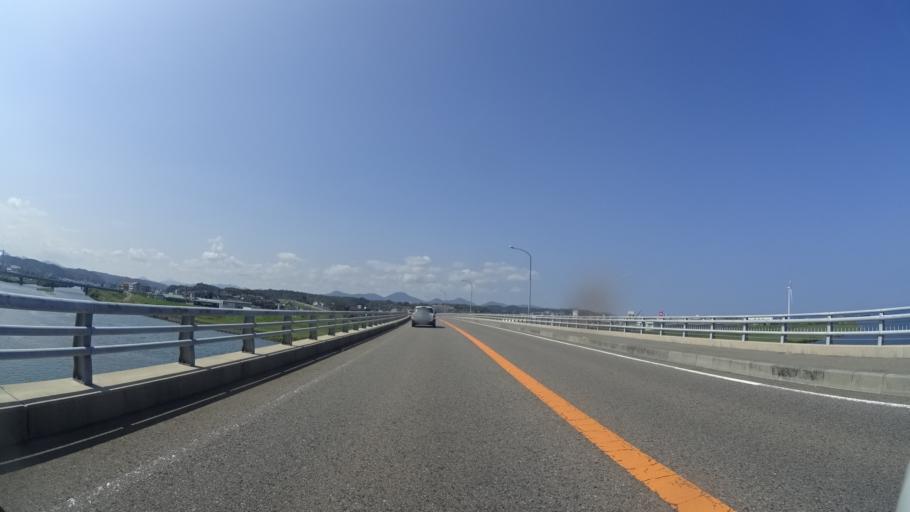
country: JP
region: Shimane
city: Masuda
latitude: 34.6909
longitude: 131.8285
